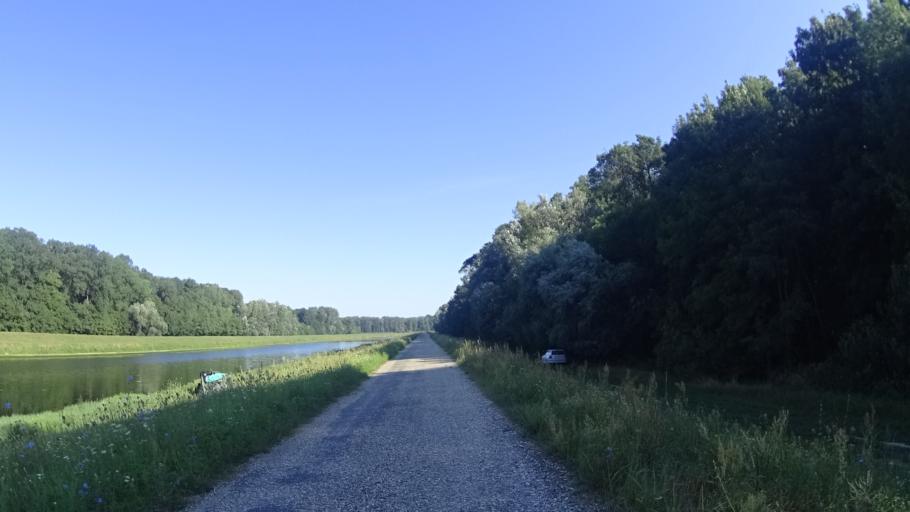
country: CZ
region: South Moravian
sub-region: Okres Breclav
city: Lanzhot
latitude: 48.6986
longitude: 16.9993
